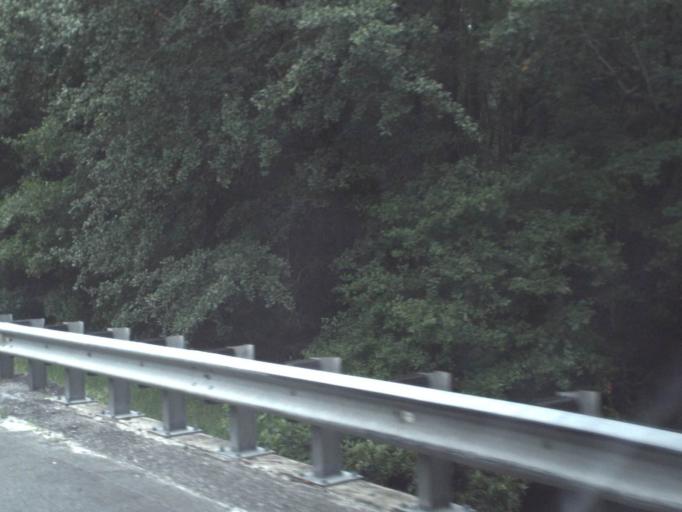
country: US
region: Florida
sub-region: Clay County
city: Middleburg
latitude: 29.9684
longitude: -81.8977
